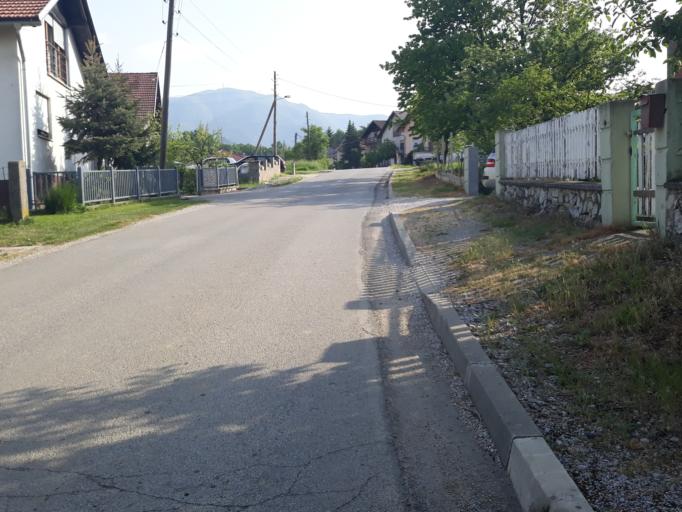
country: HR
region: Varazdinska
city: Ivanec
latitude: 46.2296
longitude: 16.1487
